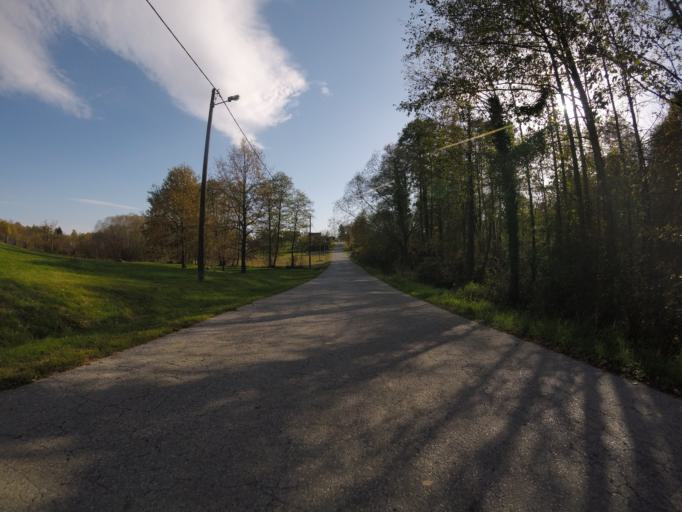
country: HR
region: Zagrebacka
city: Mraclin
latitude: 45.6168
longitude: 16.0723
